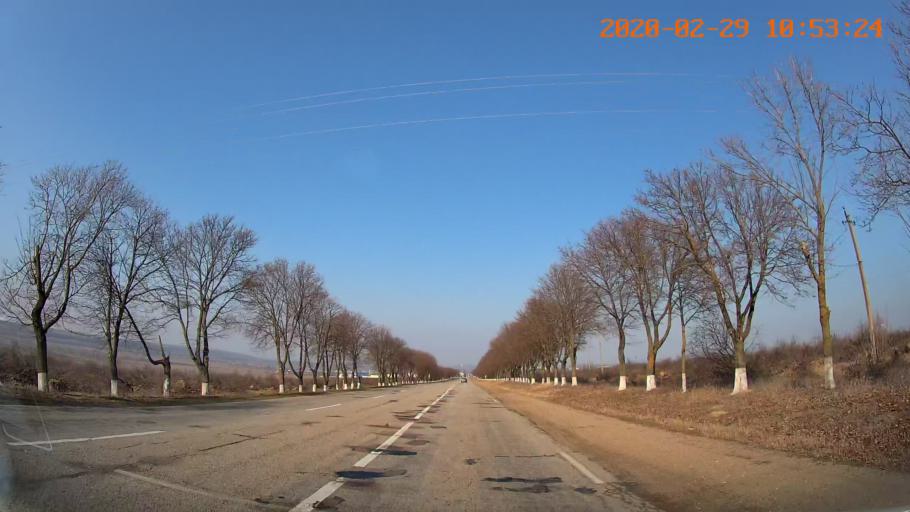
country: MD
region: Telenesti
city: Grigoriopol
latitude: 47.1156
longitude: 29.3364
